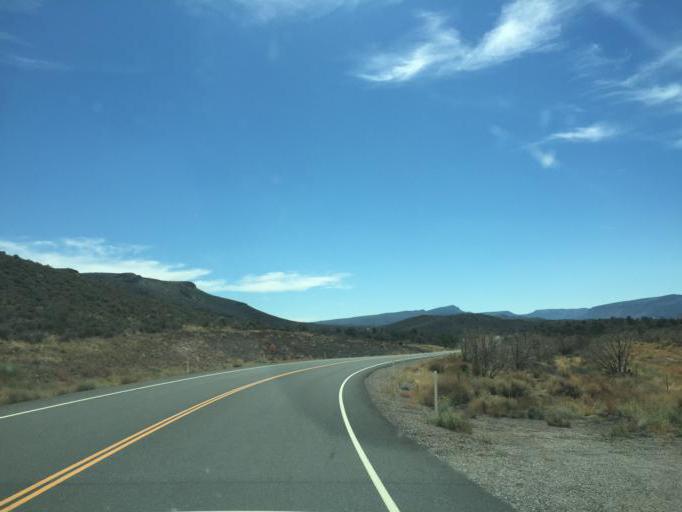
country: US
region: Arizona
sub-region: Mohave County
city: Meadview
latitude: 35.9297
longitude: -113.9061
